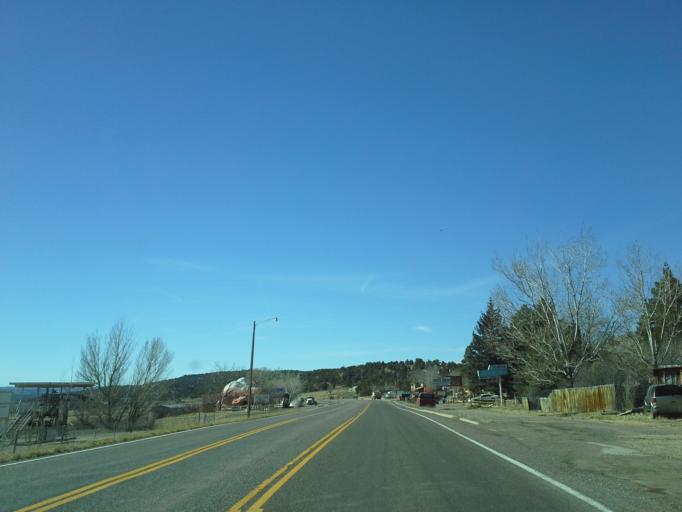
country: US
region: Utah
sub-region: Kane County
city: Kanab
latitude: 37.2729
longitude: -112.6468
